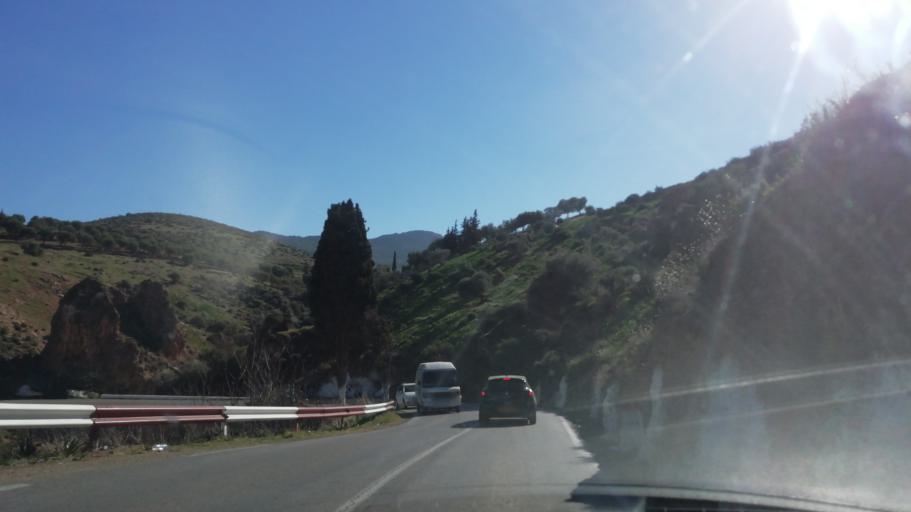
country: DZ
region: Tlemcen
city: Beni Mester
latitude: 34.8324
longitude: -1.4972
